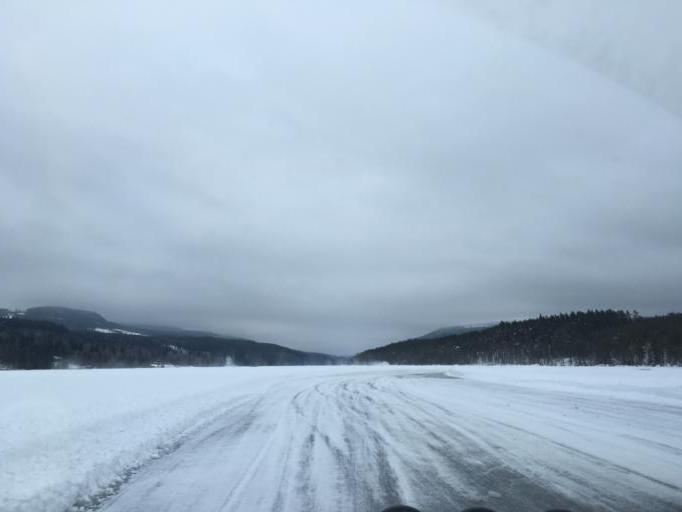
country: SE
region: Dalarna
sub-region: Alvdalens Kommun
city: AElvdalen
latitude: 61.2574
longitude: 14.0907
